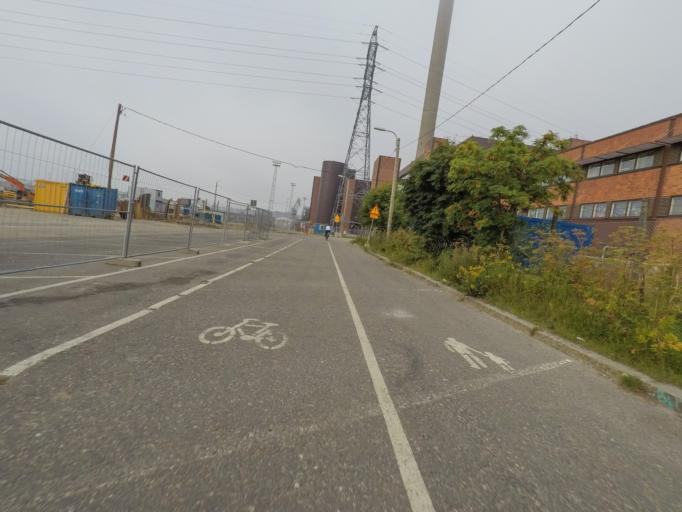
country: FI
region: Uusimaa
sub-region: Helsinki
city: Helsinki
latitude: 60.1847
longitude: 24.9748
